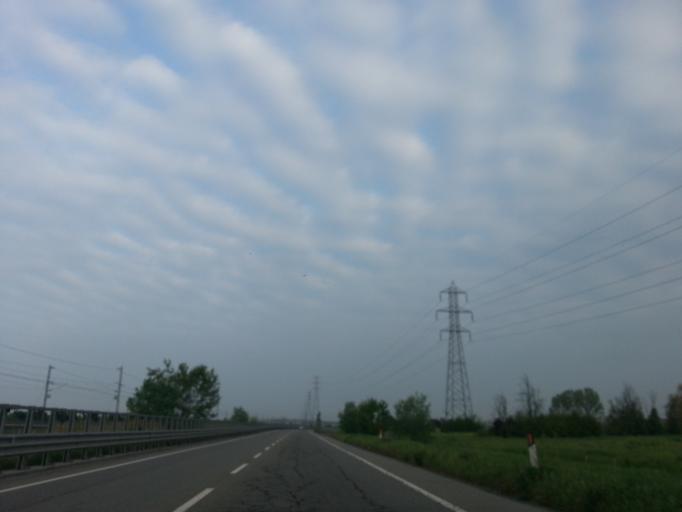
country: IT
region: Emilia-Romagna
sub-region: Provincia di Reggio Emilia
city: Massenzatico
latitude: 44.7118
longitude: 10.7167
